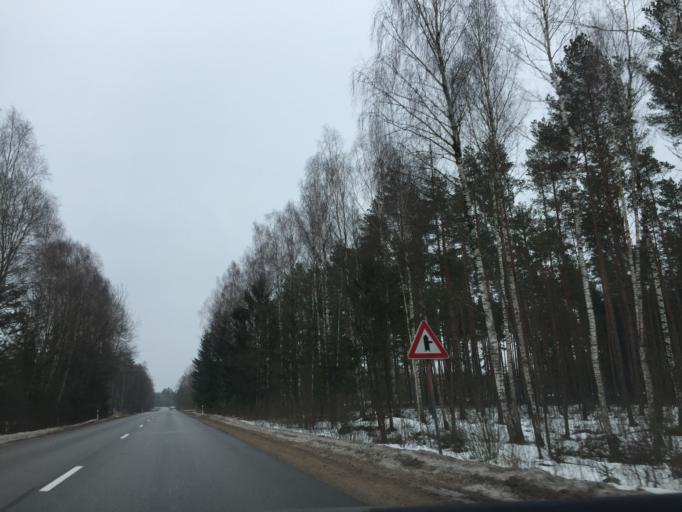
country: LV
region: Lecava
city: Iecava
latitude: 56.6102
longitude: 24.0357
